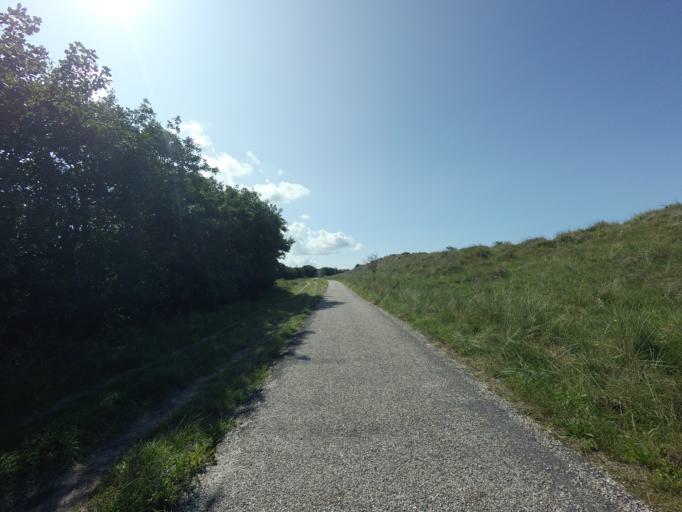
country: NL
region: Friesland
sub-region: Gemeente Terschelling
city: West-Terschelling
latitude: 53.4065
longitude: 5.3874
